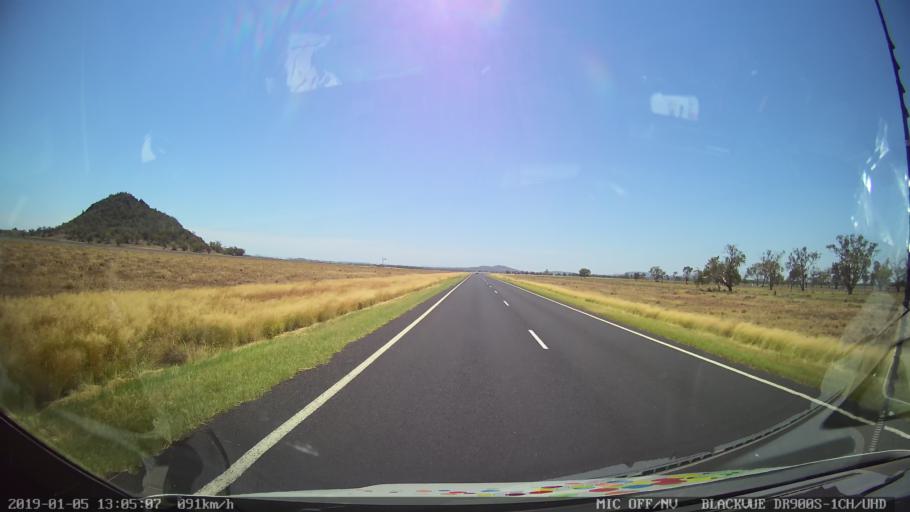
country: AU
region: New South Wales
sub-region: Gunnedah
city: Gunnedah
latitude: -31.0978
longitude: 149.8490
